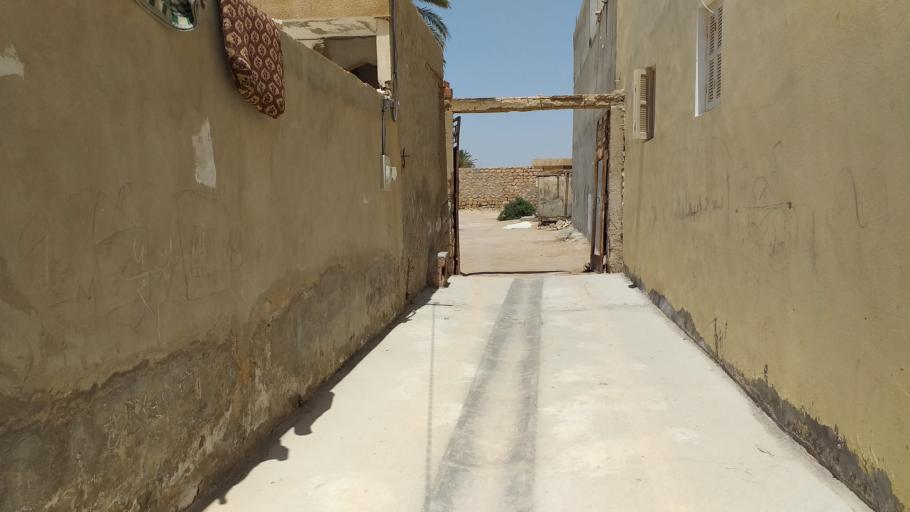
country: TN
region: Qabis
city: Gabes
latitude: 33.9424
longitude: 10.0570
